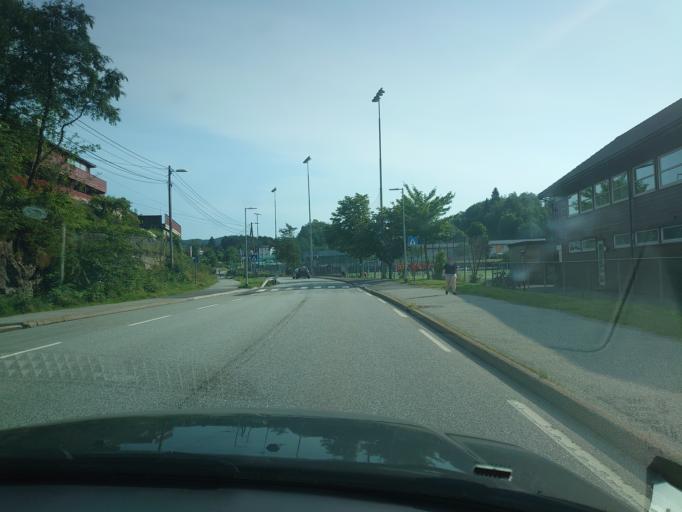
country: NO
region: Hordaland
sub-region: Bergen
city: Bergen
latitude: 60.3717
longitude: 5.3037
